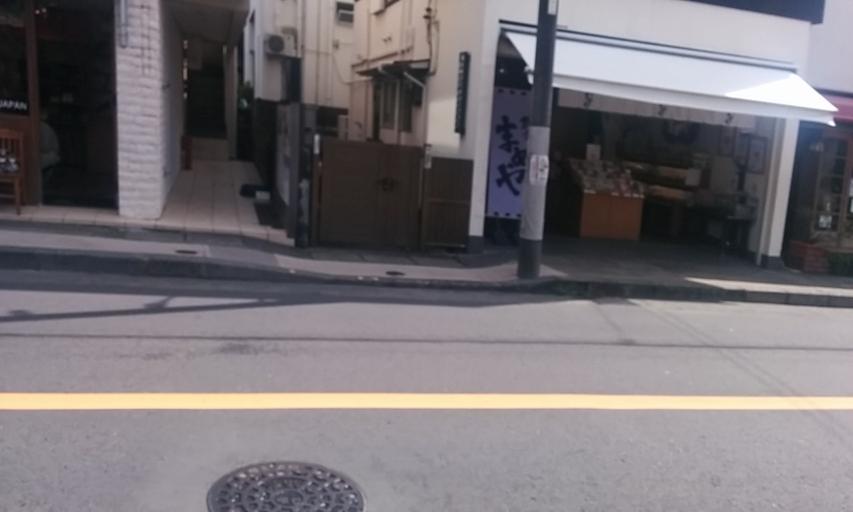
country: JP
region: Kanagawa
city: Kamakura
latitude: 35.3120
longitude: 139.5355
